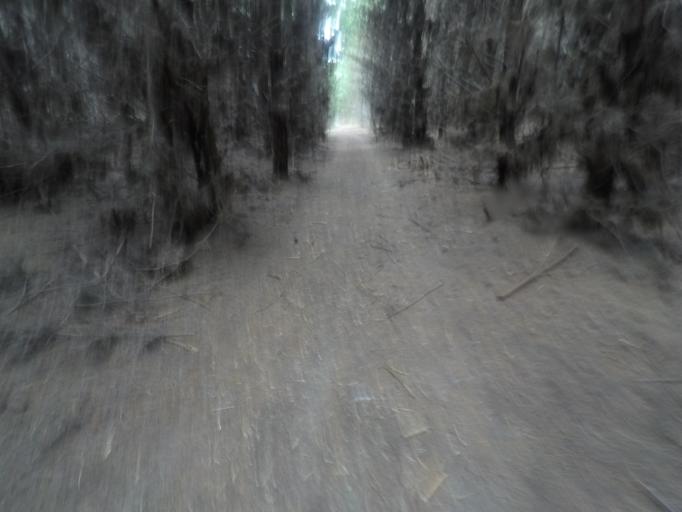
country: NZ
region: Auckland
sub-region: Auckland
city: Parakai
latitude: -36.6023
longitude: 174.2733
